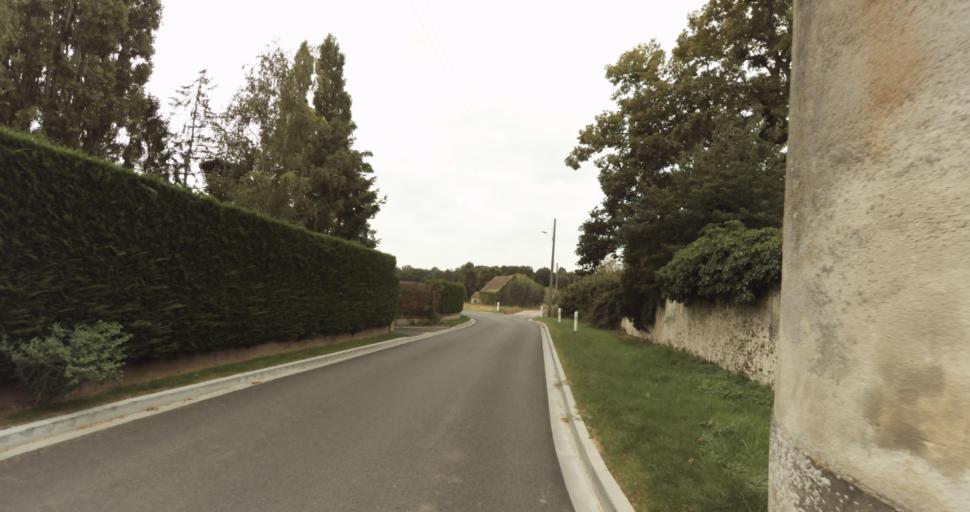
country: FR
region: Haute-Normandie
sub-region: Departement de l'Eure
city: Saint-Germain-sur-Avre
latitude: 48.8161
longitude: 1.2889
